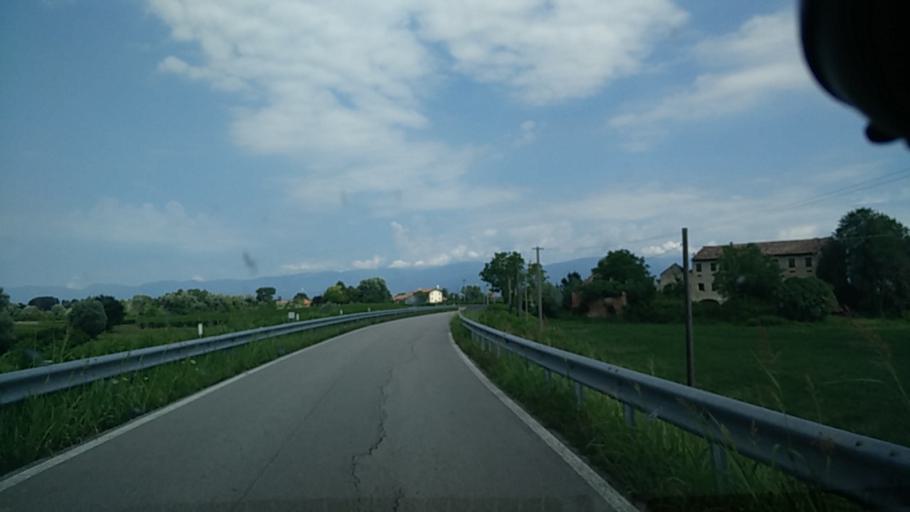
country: IT
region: Friuli Venezia Giulia
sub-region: Provincia di Pordenone
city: Puia-Villanova
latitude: 45.8490
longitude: 12.5570
